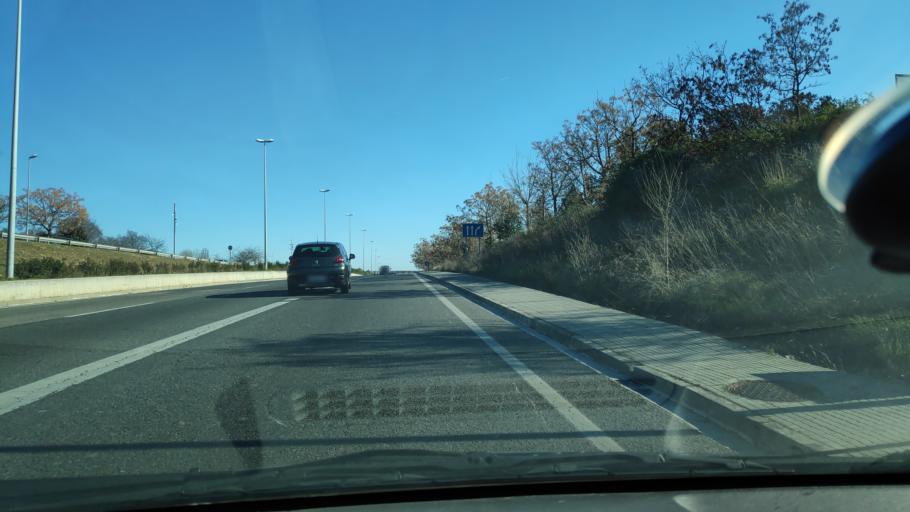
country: ES
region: Catalonia
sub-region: Provincia de Barcelona
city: Terrassa
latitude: 41.5567
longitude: 2.0412
